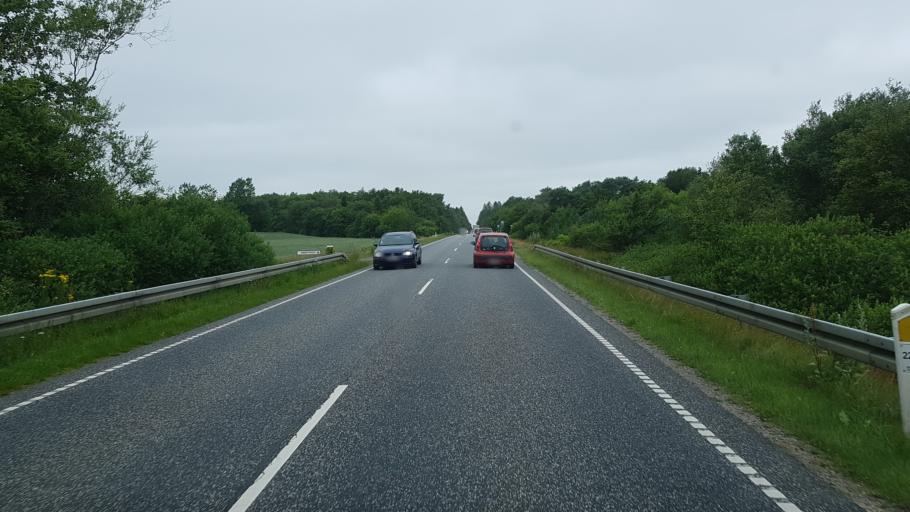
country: DK
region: Central Jutland
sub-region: Lemvig Kommune
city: Lemvig
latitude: 56.4608
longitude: 8.3302
